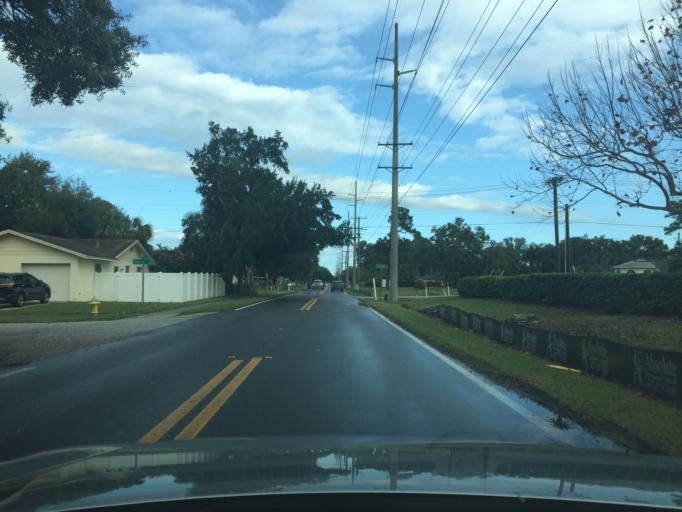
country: US
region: Florida
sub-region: Hillsborough County
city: Town 'n' Country
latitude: 27.9850
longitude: -82.5505
